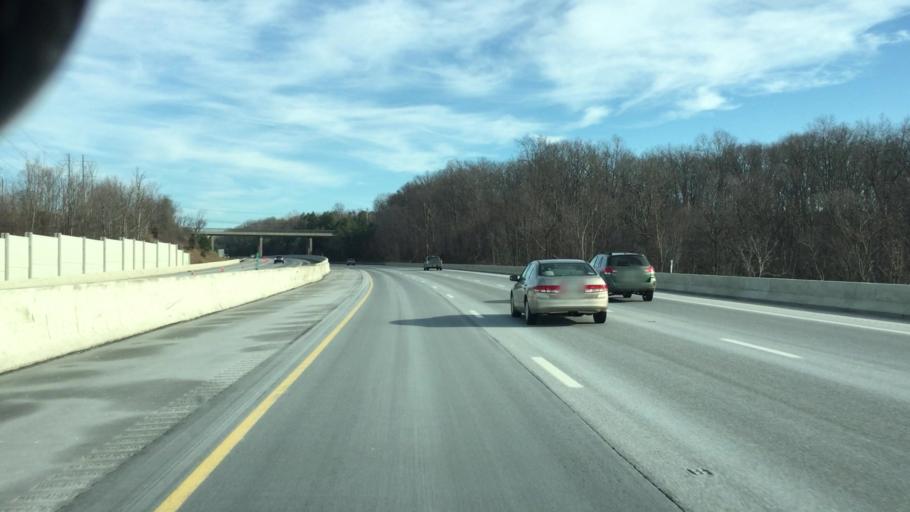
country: US
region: Ohio
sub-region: Cuyahoga County
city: North Royalton
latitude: 41.3042
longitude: -81.7409
